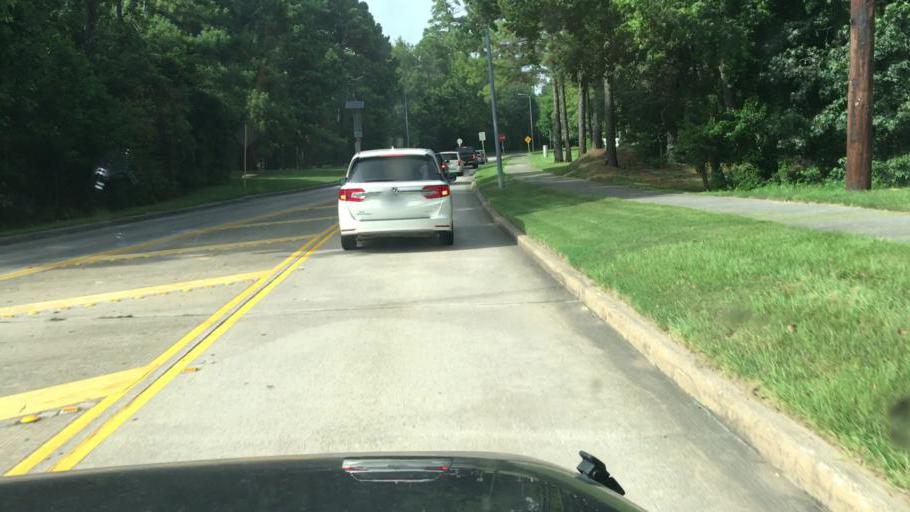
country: US
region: Texas
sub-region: Harris County
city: Atascocita
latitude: 30.0017
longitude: -95.1778
